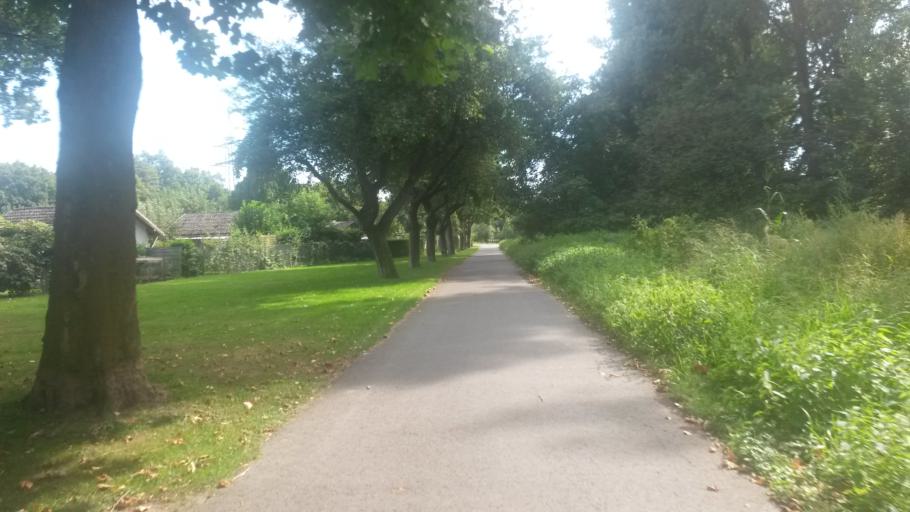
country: DE
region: North Rhine-Westphalia
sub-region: Regierungsbezirk Detmold
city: Paderborn
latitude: 51.7128
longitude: 8.7180
